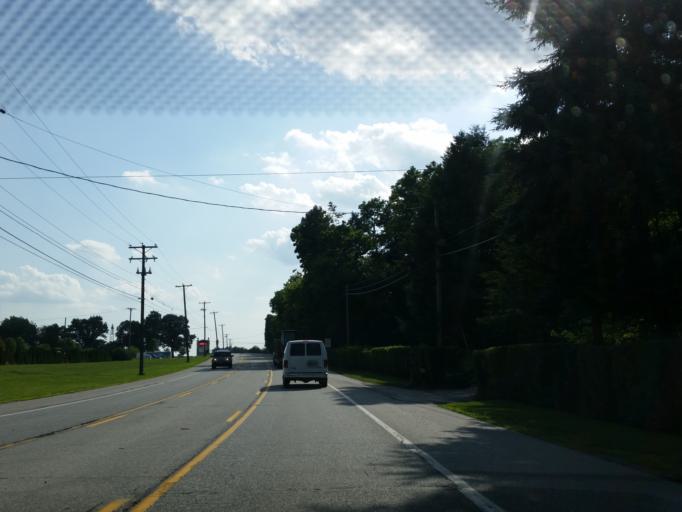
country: US
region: Pennsylvania
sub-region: York County
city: Hallam
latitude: 40.0014
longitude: -76.6192
